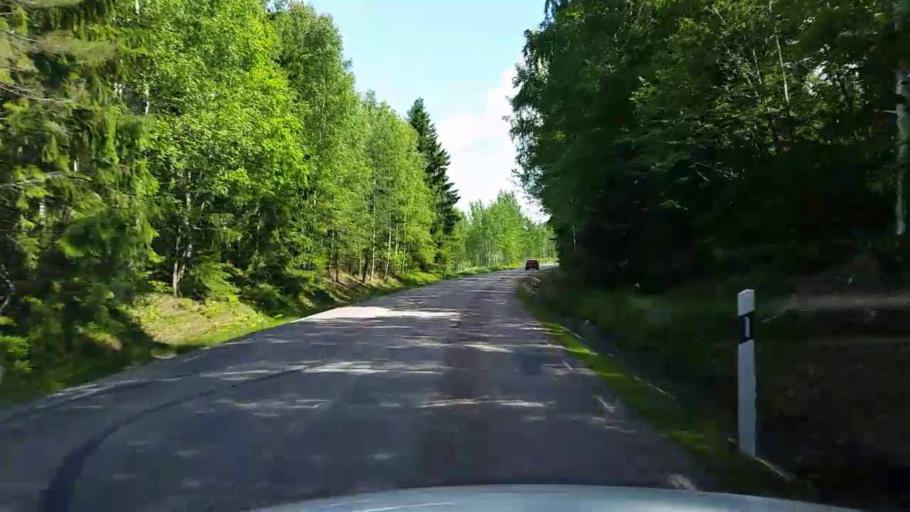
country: SE
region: Vaestmanland
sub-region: Kopings Kommun
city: Kolsva
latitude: 59.7010
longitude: 15.7867
